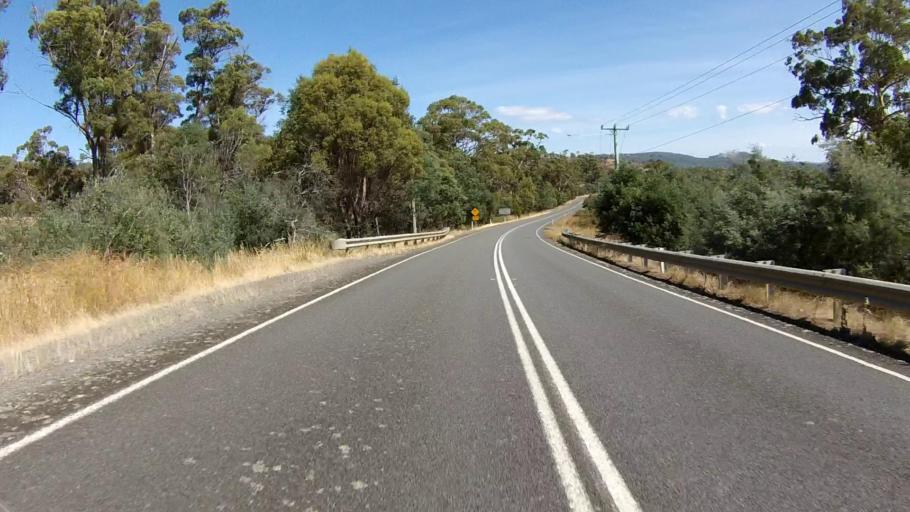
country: AU
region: Tasmania
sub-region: Sorell
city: Sorell
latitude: -42.5884
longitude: 147.7997
